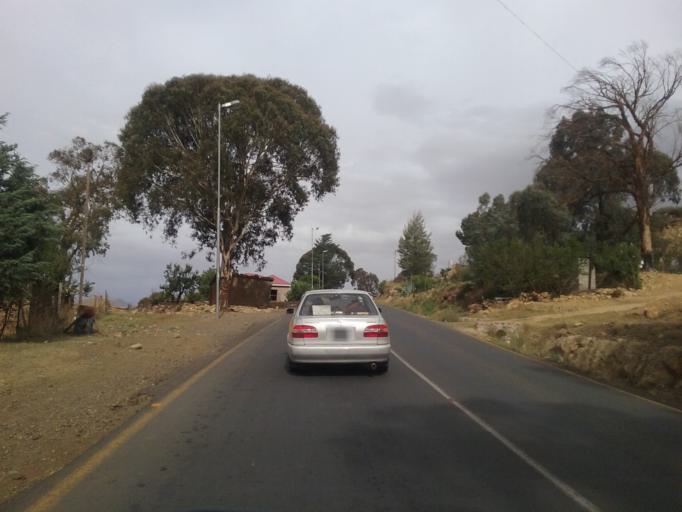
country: LS
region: Quthing
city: Quthing
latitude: -30.4027
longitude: 27.7065
